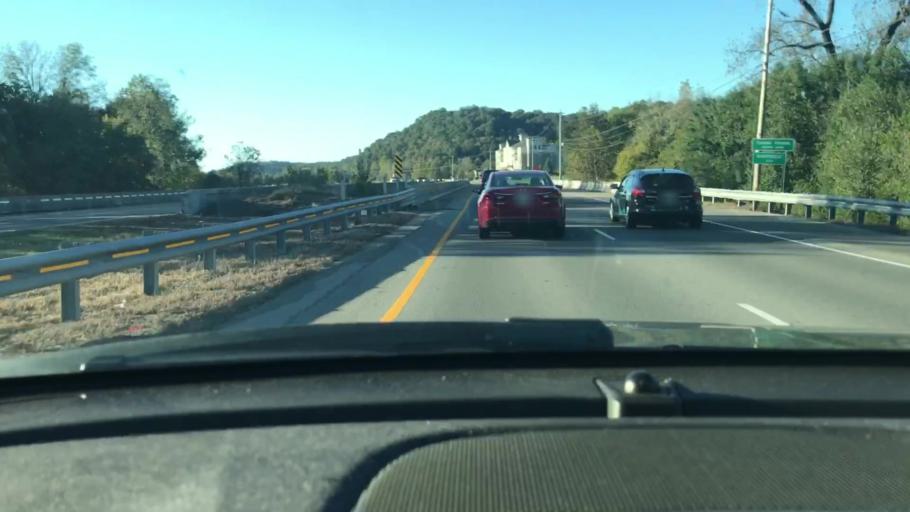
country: US
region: Tennessee
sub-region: Cheatham County
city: Ashland City
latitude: 36.2412
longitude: -87.0233
